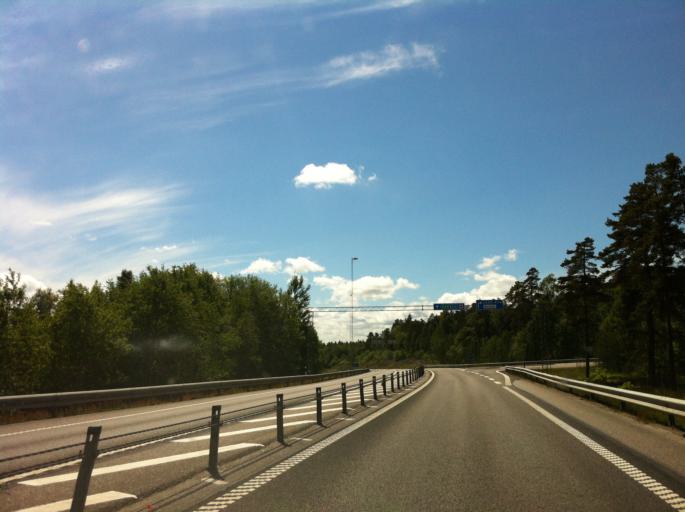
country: SE
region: Vaestra Goetaland
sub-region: Vanersborgs Kommun
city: Vanersborg
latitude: 58.3826
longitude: 12.2841
